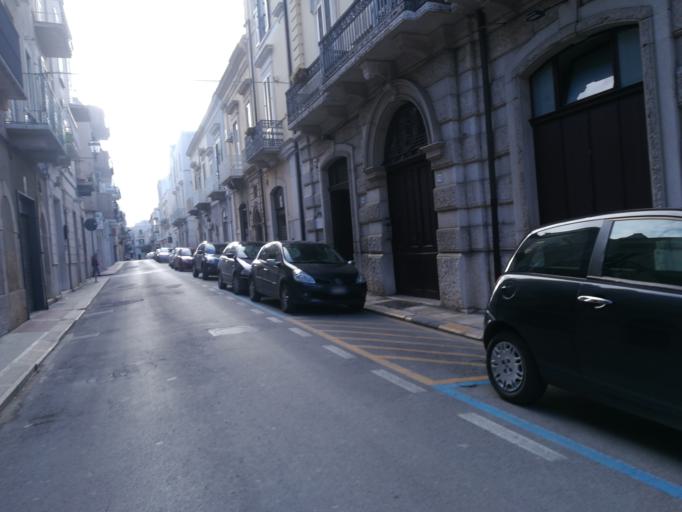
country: IT
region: Apulia
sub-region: Provincia di Barletta - Andria - Trani
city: Andria
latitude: 41.2267
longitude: 16.3013
